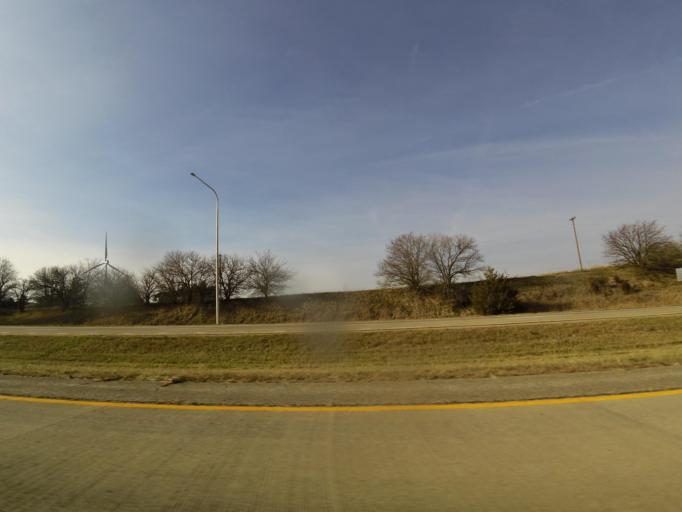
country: US
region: Illinois
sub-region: Macon County
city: Maroa
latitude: 40.0386
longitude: -88.9651
